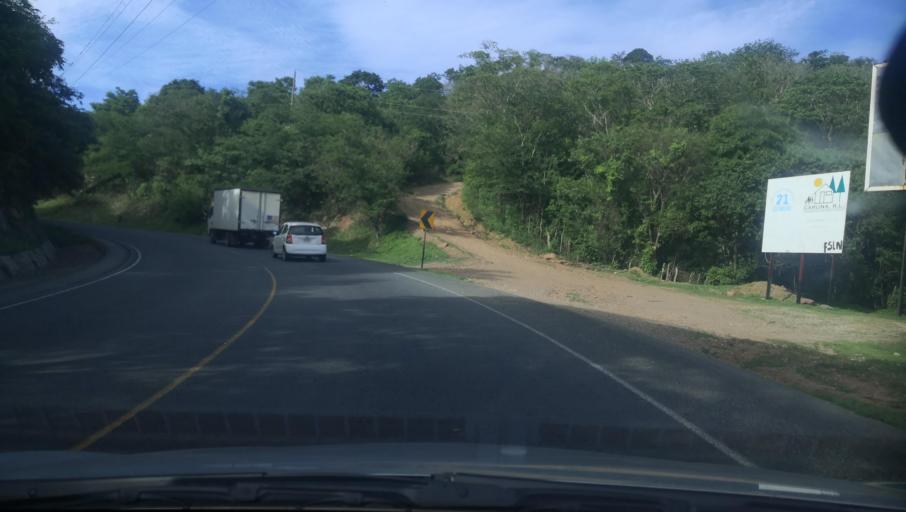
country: NI
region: Madriz
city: Totogalpa
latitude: 13.5863
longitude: -86.4744
